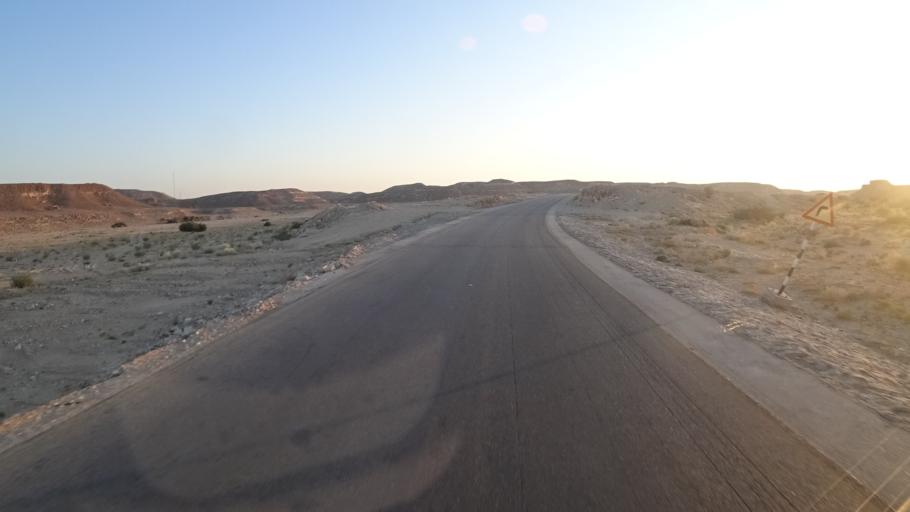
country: OM
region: Zufar
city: Salalah
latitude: 17.4946
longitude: 53.3621
